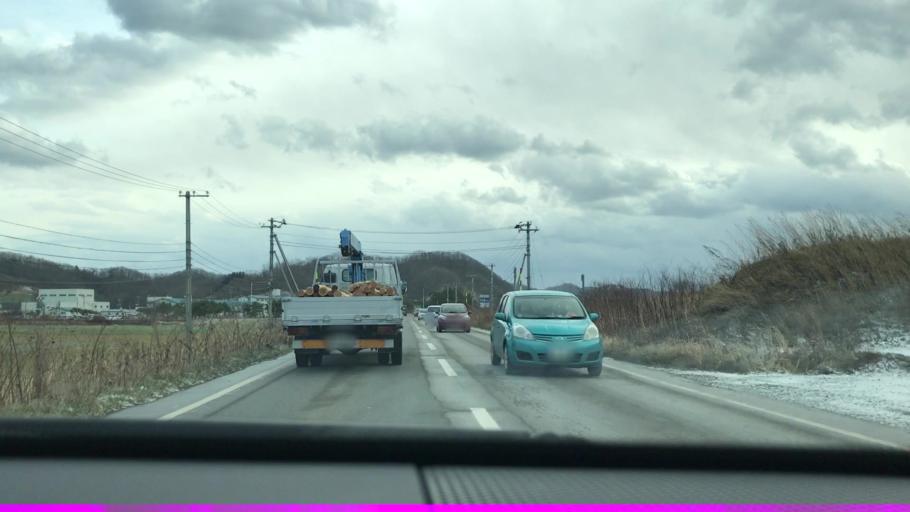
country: JP
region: Hokkaido
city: Shizunai-furukawacho
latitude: 42.3091
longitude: 142.4332
